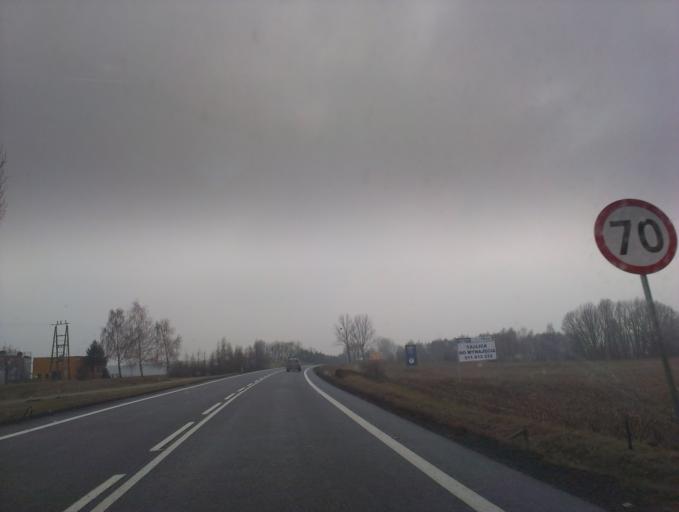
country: PL
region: Greater Poland Voivodeship
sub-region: Powiat poznanski
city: Zlotniki
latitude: 52.5456
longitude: 16.8399
